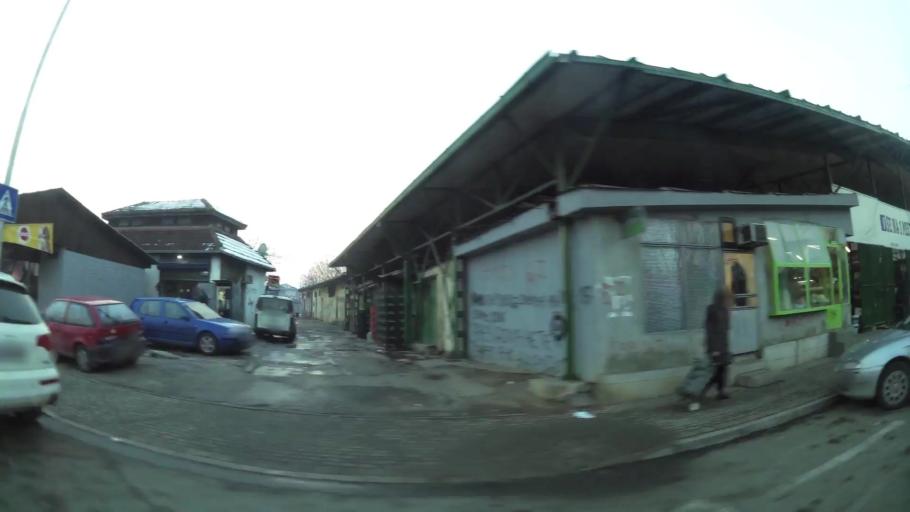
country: MK
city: Creshevo
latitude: 42.0045
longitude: 21.5041
